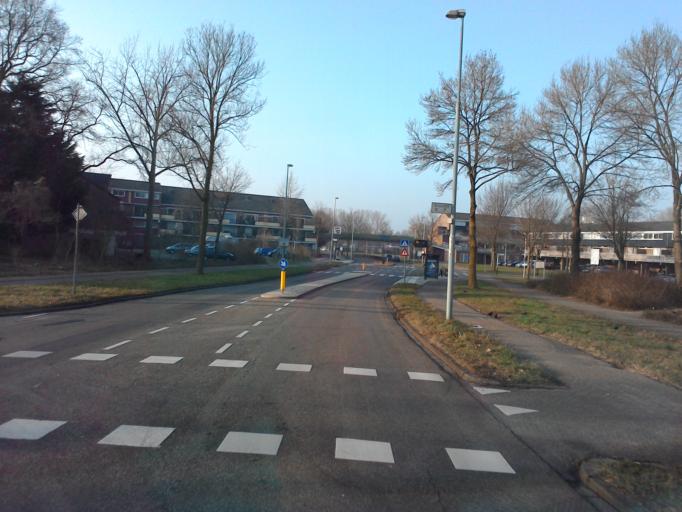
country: NL
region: Utrecht
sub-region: Gemeente Zeist
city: Zeist
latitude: 52.0813
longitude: 5.2169
